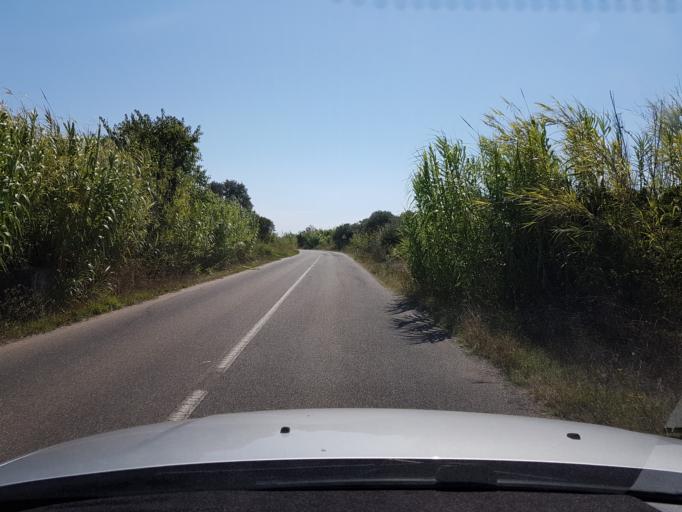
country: IT
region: Sardinia
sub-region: Provincia di Oristano
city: Nurachi
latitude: 39.9556
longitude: 8.5335
